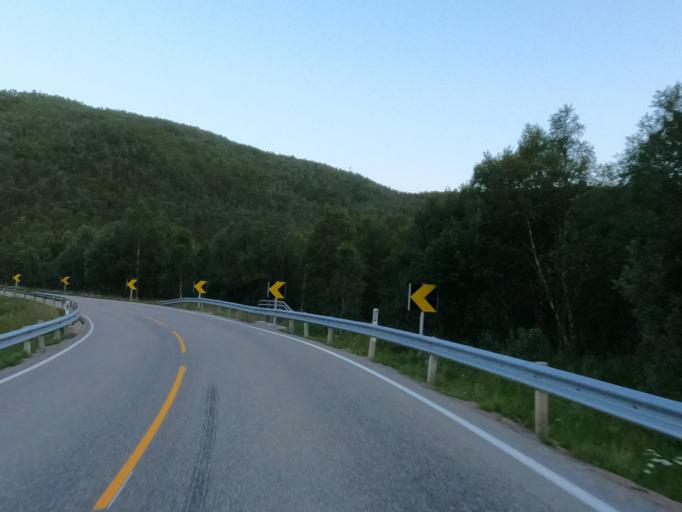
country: NO
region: Nordland
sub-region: Lodingen
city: Lodingen
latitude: 68.4927
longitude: 16.0813
